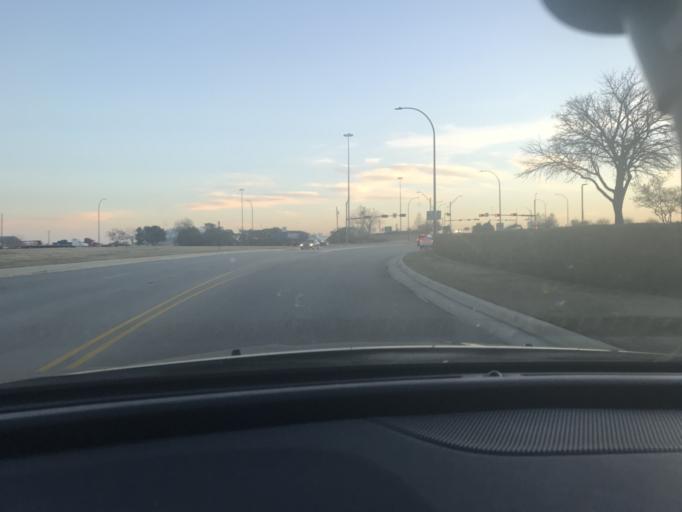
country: US
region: Texas
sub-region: Tarrant County
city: Arlington
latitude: 32.7629
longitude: -97.1018
